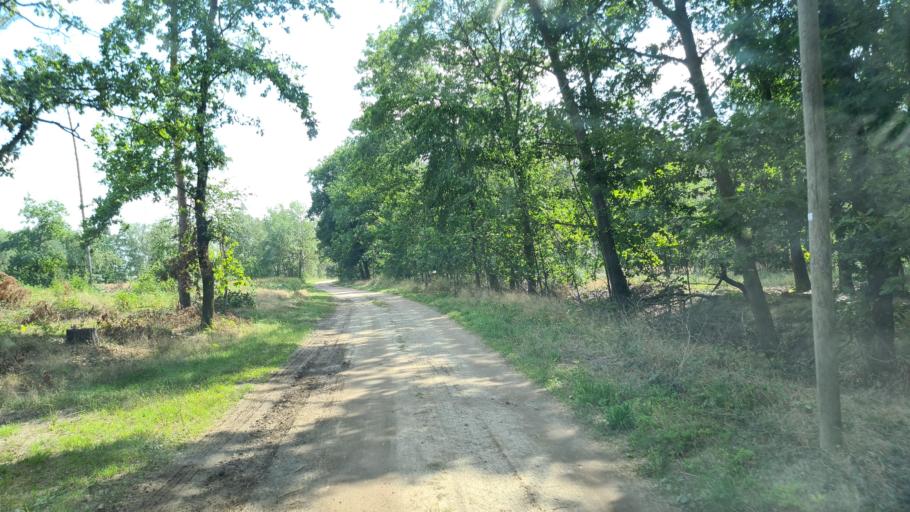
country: DE
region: Brandenburg
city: Sonnewalde
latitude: 51.7288
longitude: 13.6486
